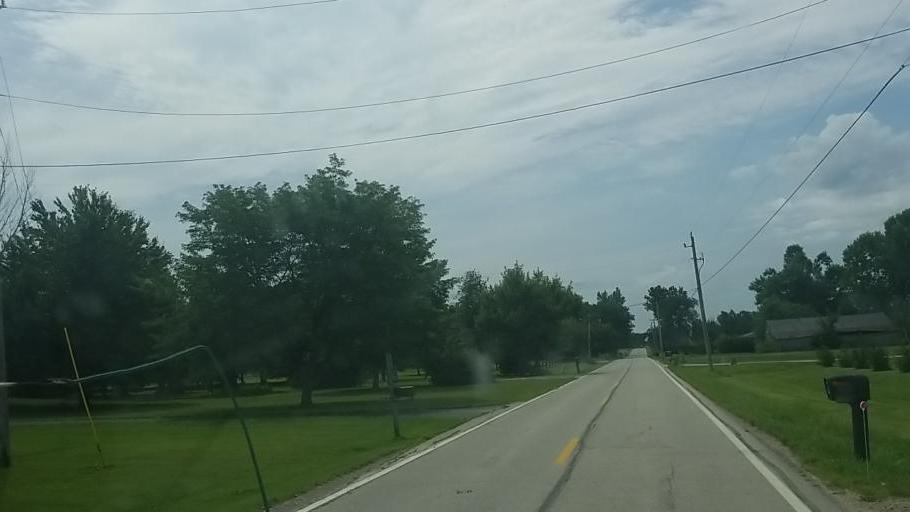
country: US
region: Ohio
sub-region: Delaware County
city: Sunbury
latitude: 40.1918
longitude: -82.8260
